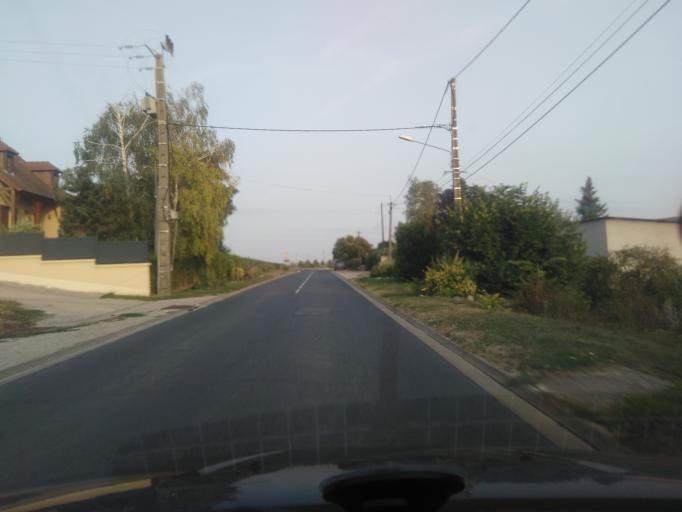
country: FR
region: Champagne-Ardenne
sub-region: Departement de la Marne
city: Mareuil-le-Port
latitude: 49.0815
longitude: 3.8038
